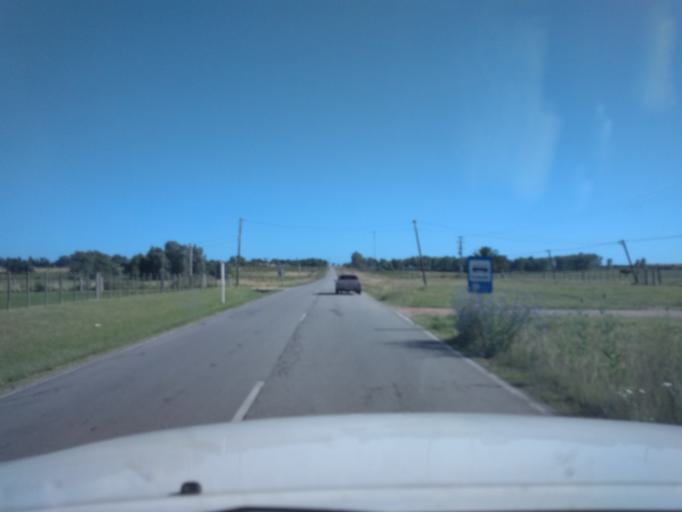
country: UY
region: Canelones
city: San Ramon
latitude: -34.3155
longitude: -55.9592
